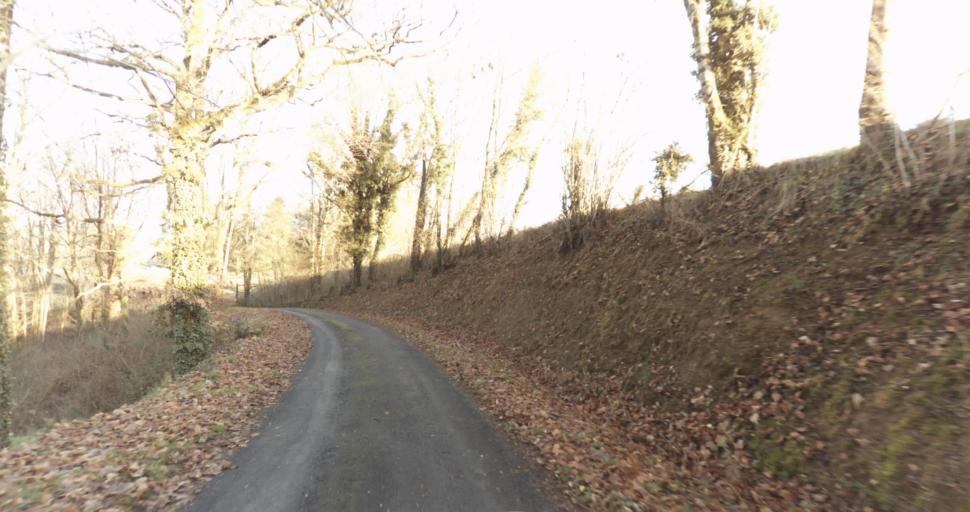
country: FR
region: Limousin
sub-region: Departement de la Haute-Vienne
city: Aixe-sur-Vienne
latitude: 45.7892
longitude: 1.1399
